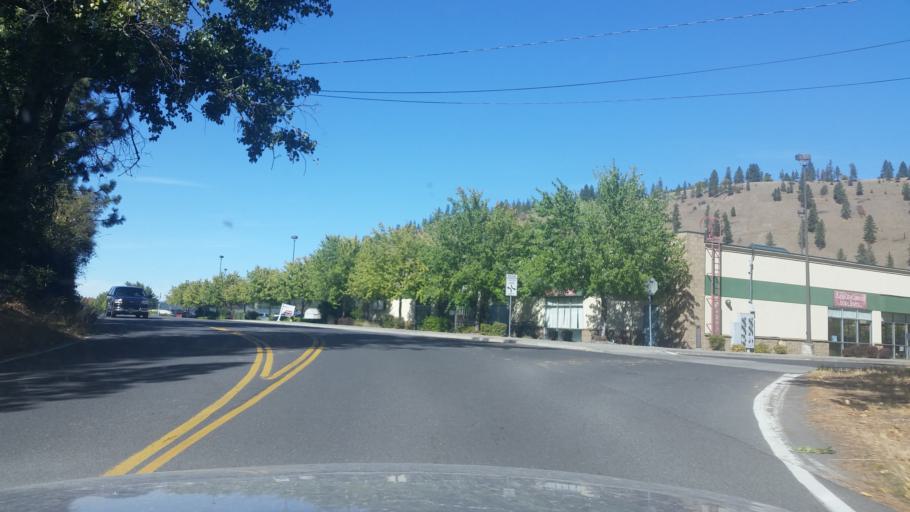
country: US
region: Washington
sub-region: Spokane County
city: Spokane
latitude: 47.6137
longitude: -117.4299
